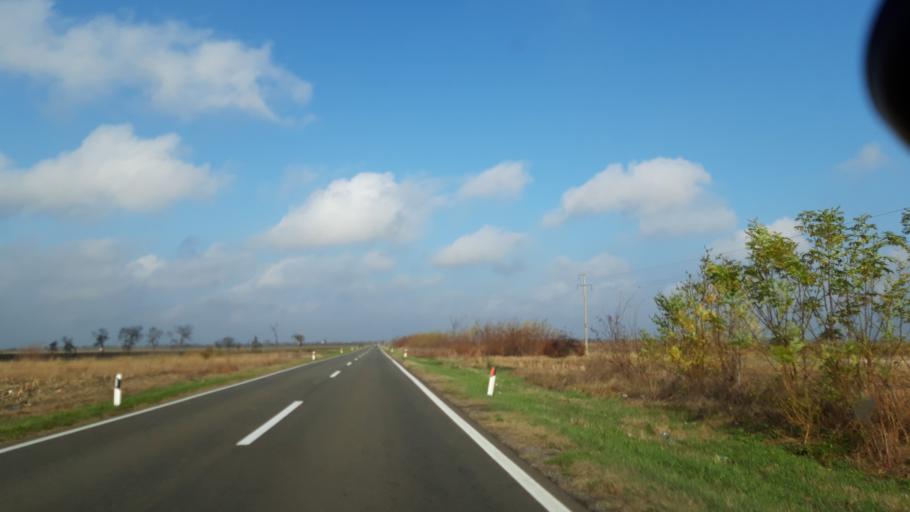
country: RS
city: Ostojicevo
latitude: 45.8692
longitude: 20.1649
